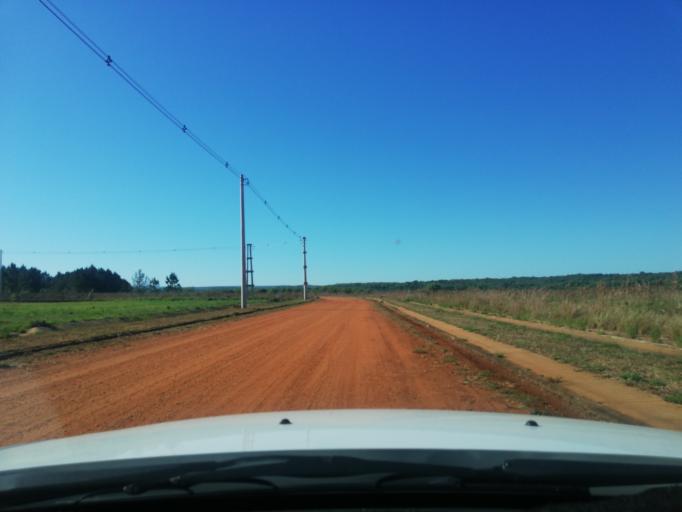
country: AR
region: Misiones
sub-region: Departamento de Candelaria
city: Candelaria
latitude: -27.4856
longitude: -55.7825
